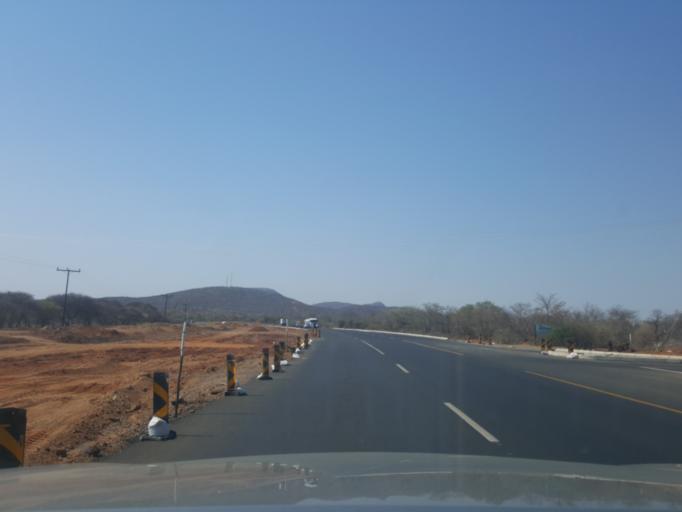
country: BW
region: South East
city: Ramotswa
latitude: -24.7696
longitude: 25.8303
